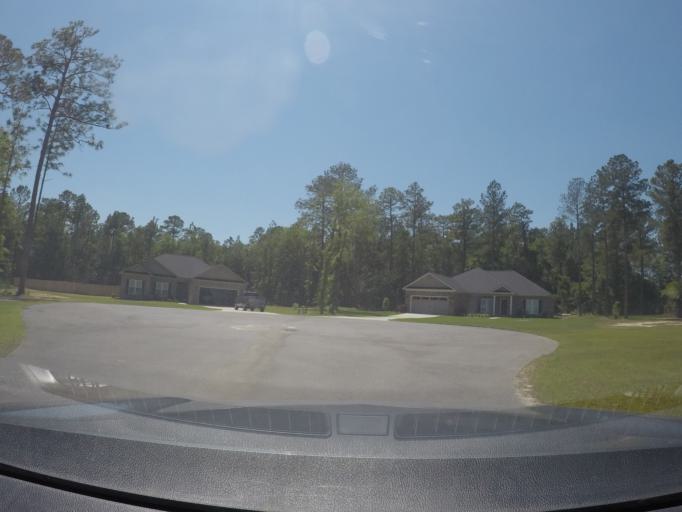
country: US
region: Georgia
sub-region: Bulloch County
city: Statesboro
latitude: 32.3540
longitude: -81.7654
